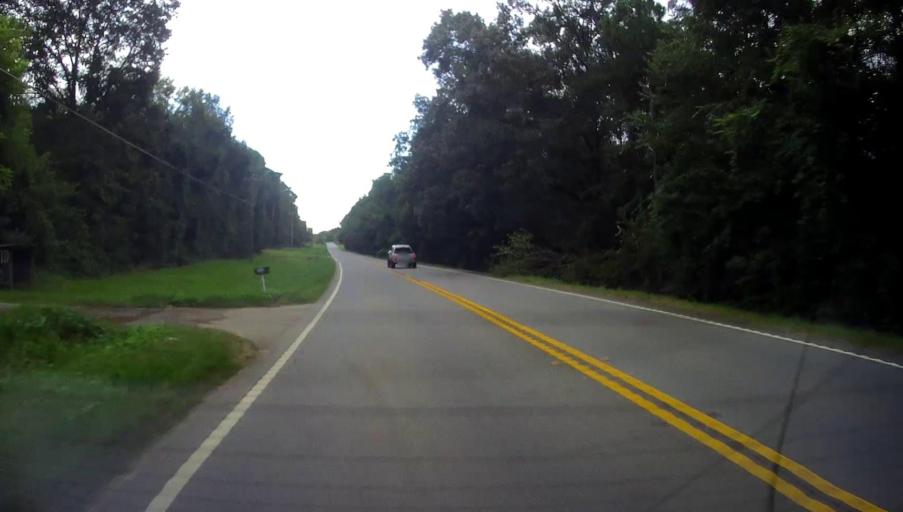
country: US
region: Georgia
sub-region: Houston County
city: Perry
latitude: 32.3992
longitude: -83.6295
